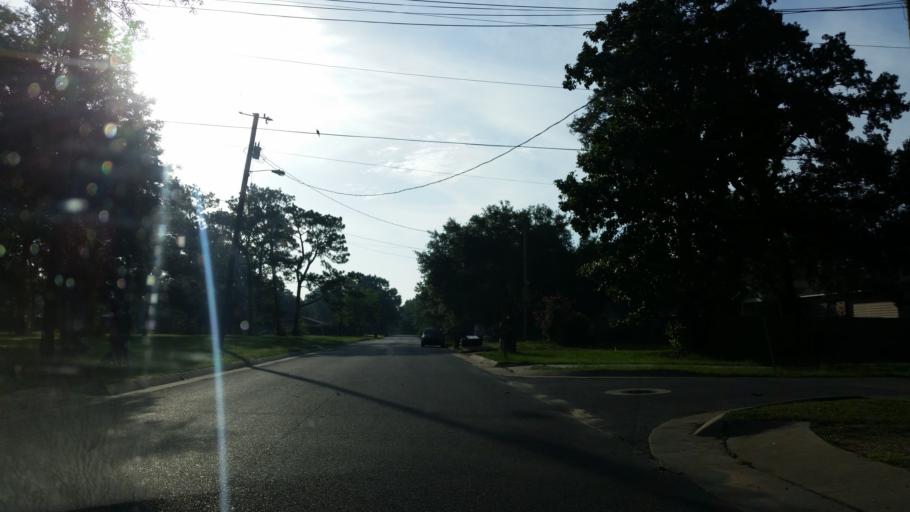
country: US
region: Florida
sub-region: Escambia County
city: Ferry Pass
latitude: 30.4899
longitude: -87.2022
